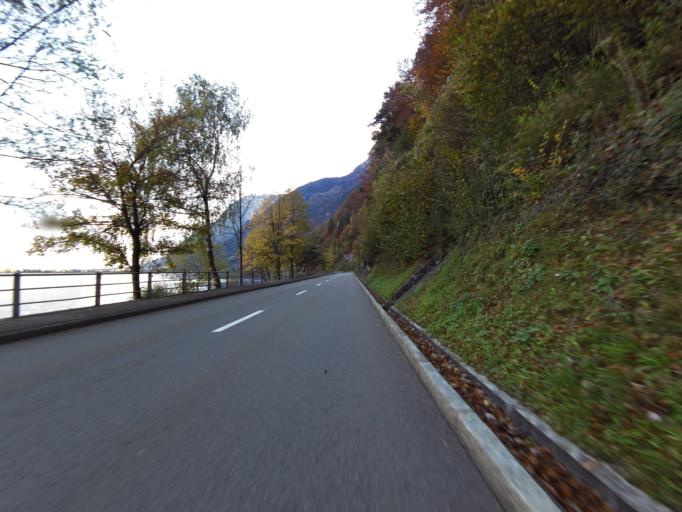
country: CH
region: Uri
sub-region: Uri
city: Flueelen
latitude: 46.9074
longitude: 8.5920
